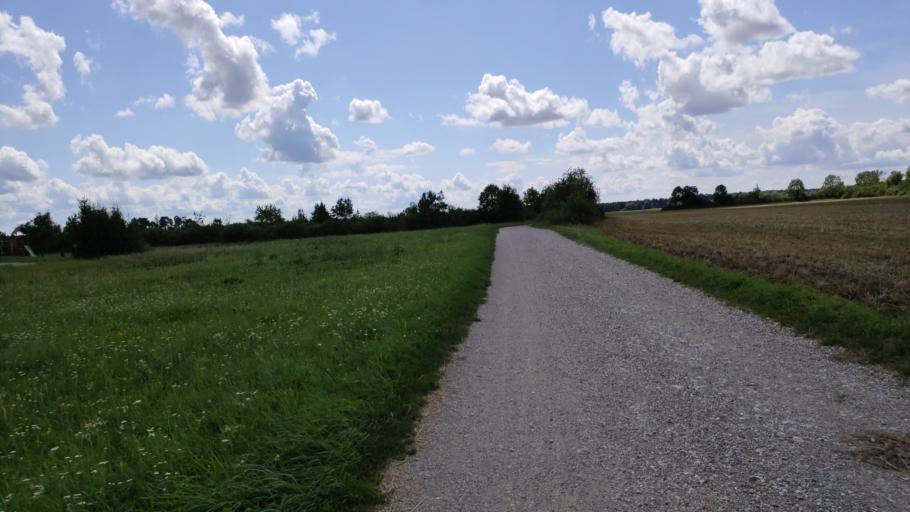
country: DE
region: Bavaria
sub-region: Upper Bavaria
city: Prittriching
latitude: 48.2319
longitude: 10.8928
